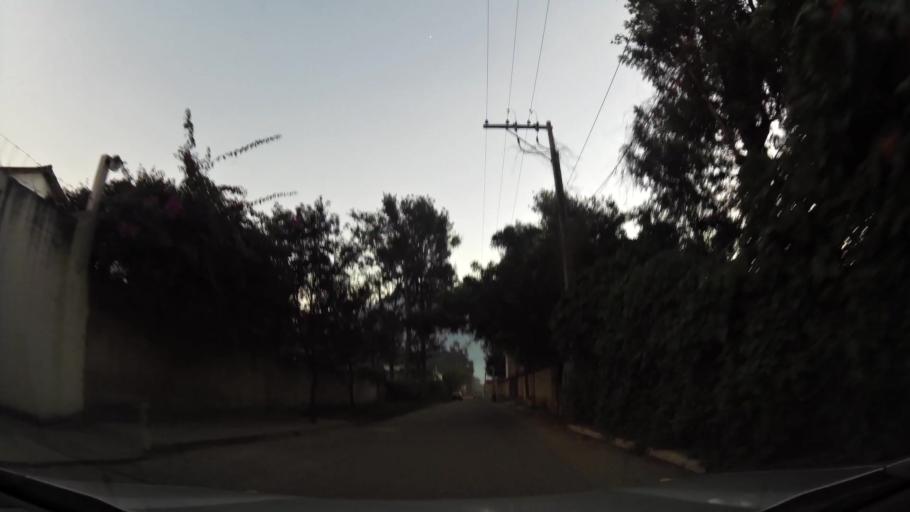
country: GT
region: Sacatepequez
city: Antigua Guatemala
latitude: 14.5465
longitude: -90.7480
